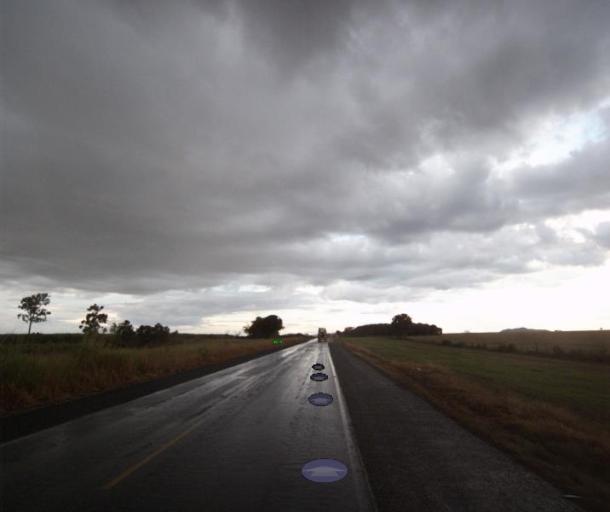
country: BR
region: Goias
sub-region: Uruacu
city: Uruacu
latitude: -14.6459
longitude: -49.1833
